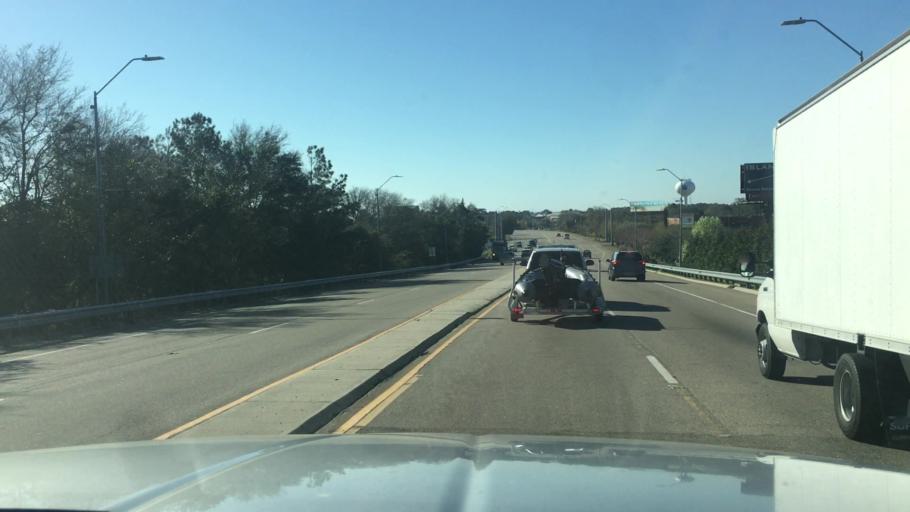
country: US
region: North Carolina
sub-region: New Hanover County
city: Sea Breeze
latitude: 34.0533
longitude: -77.8997
